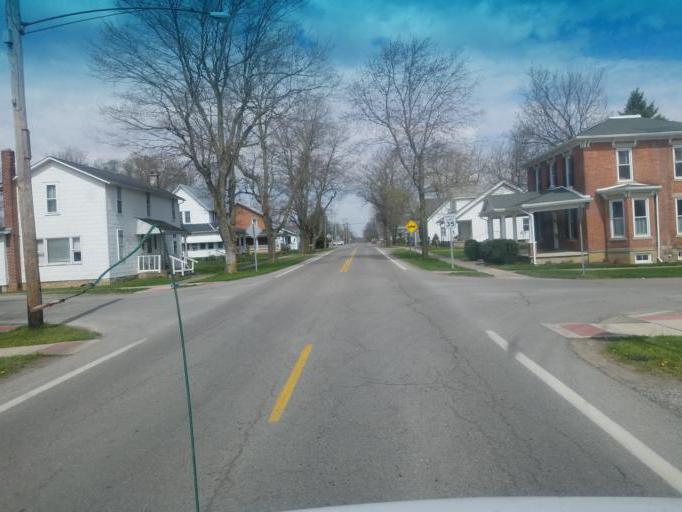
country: US
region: Ohio
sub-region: Logan County
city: Northwood
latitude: 40.5075
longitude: -83.7496
